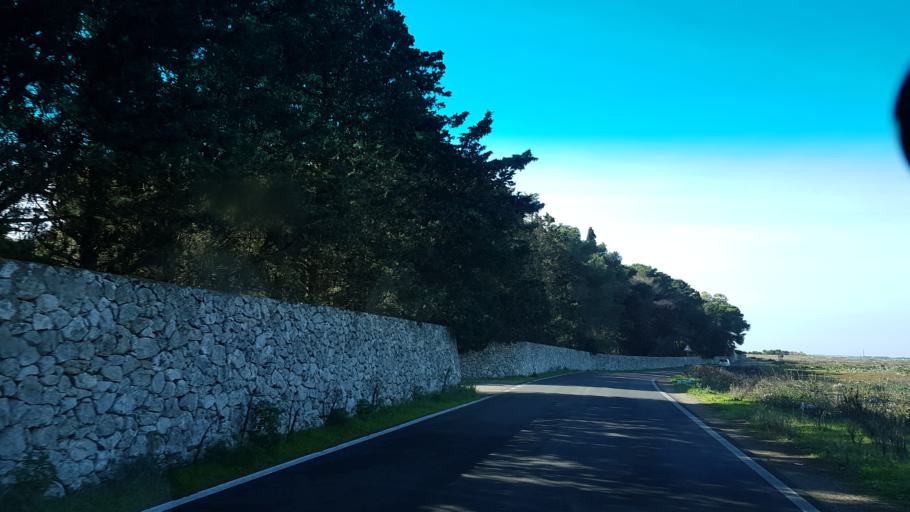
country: IT
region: Apulia
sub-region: Provincia di Lecce
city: Lecce
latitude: 40.3494
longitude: 18.1398
